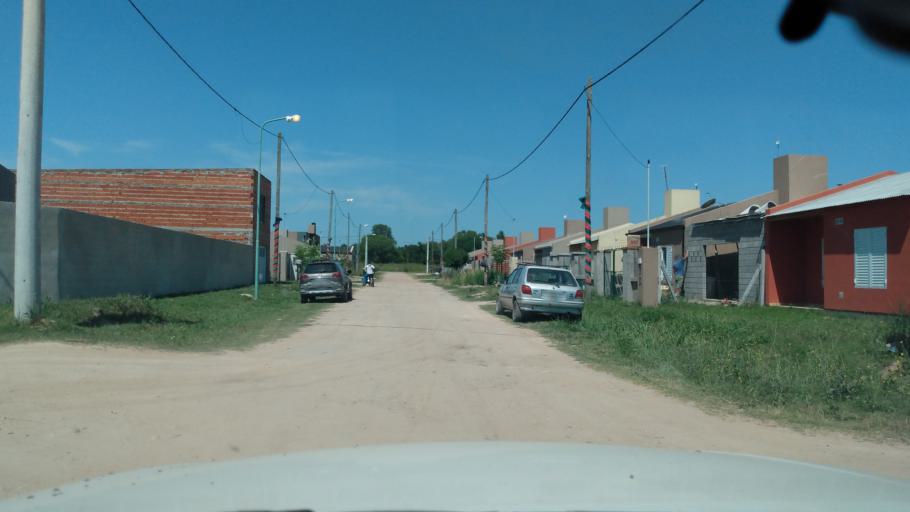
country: AR
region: Buenos Aires
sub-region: Partido de Lujan
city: Lujan
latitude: -34.5537
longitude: -59.1371
